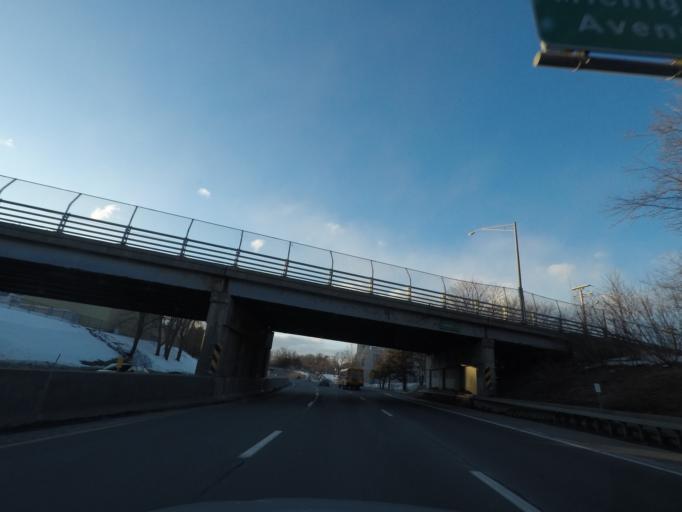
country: US
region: New York
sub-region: Schenectady County
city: Schenectady
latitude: 42.7960
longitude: -73.9282
